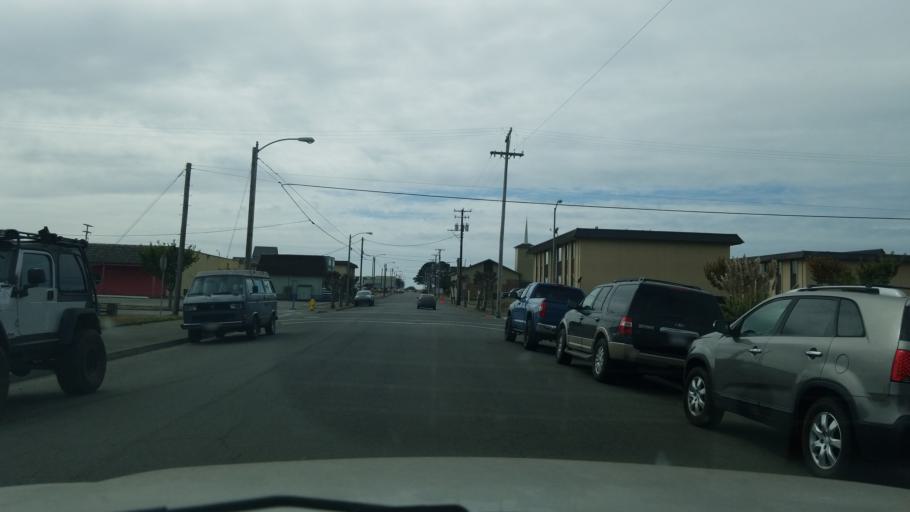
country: US
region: California
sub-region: Del Norte County
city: Crescent City
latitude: 41.7513
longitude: -124.1977
